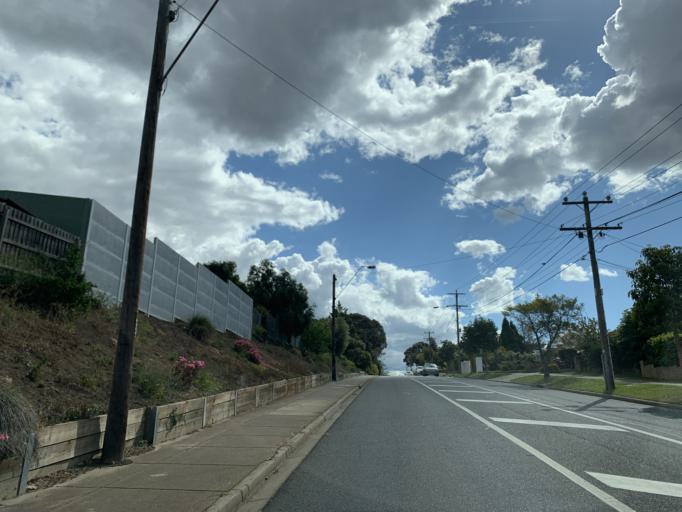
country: AU
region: Victoria
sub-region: Moonee Valley
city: Essendon West
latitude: -37.7475
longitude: 144.8782
